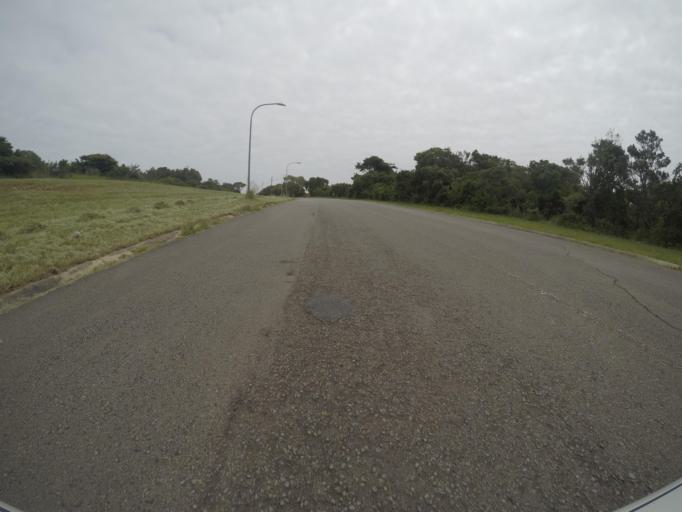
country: ZA
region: Eastern Cape
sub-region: Buffalo City Metropolitan Municipality
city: East London
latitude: -32.9743
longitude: 27.9453
